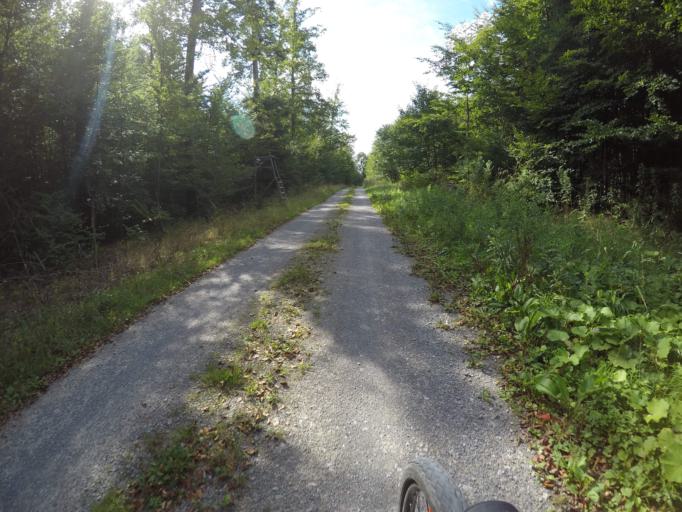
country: DE
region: Baden-Wuerttemberg
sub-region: Karlsruhe Region
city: Gechingen
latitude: 48.6773
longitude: 8.8215
